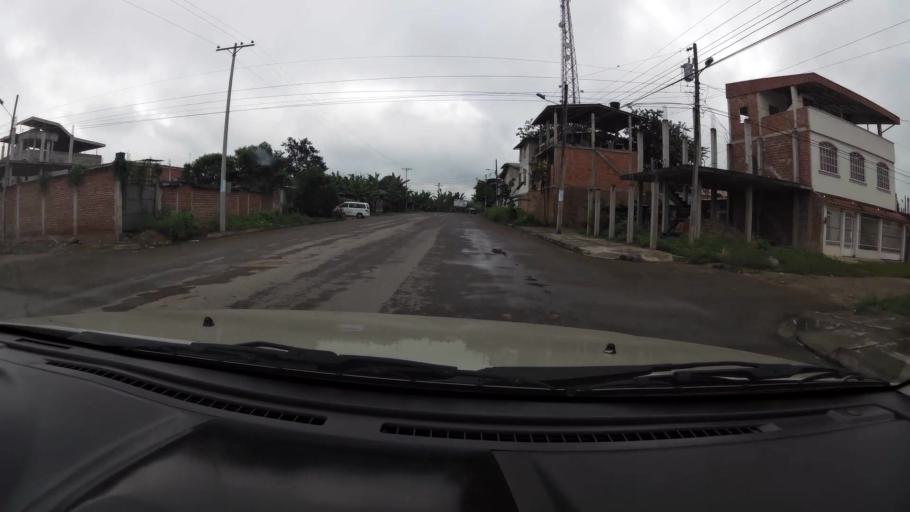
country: EC
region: El Oro
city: Pasaje
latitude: -3.3208
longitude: -79.8113
